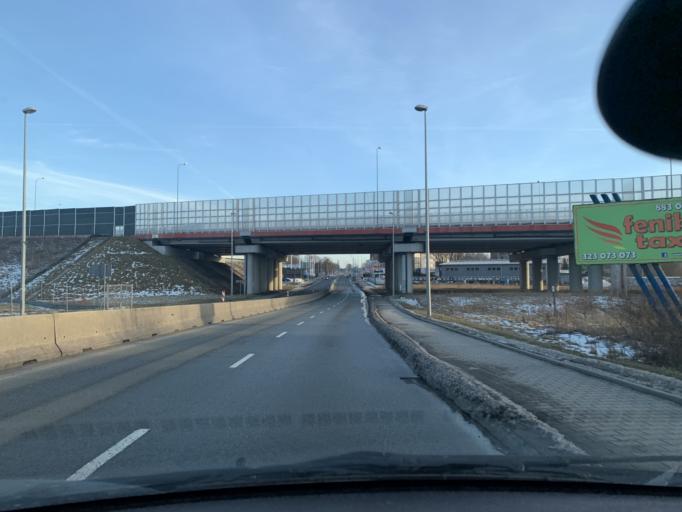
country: PL
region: Silesian Voivodeship
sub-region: Powiat tarnogorski
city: Radzionkow
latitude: 50.3736
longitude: 18.8922
